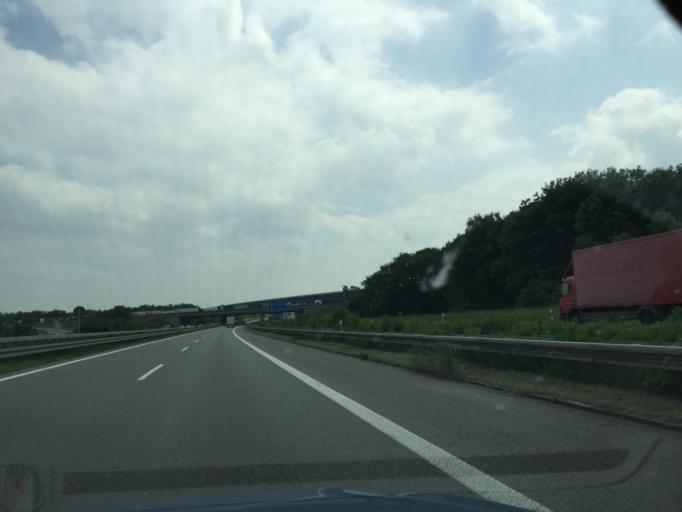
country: DE
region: Baden-Wuerttemberg
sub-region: Tuebingen Region
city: Langenau
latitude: 48.4680
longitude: 10.1142
